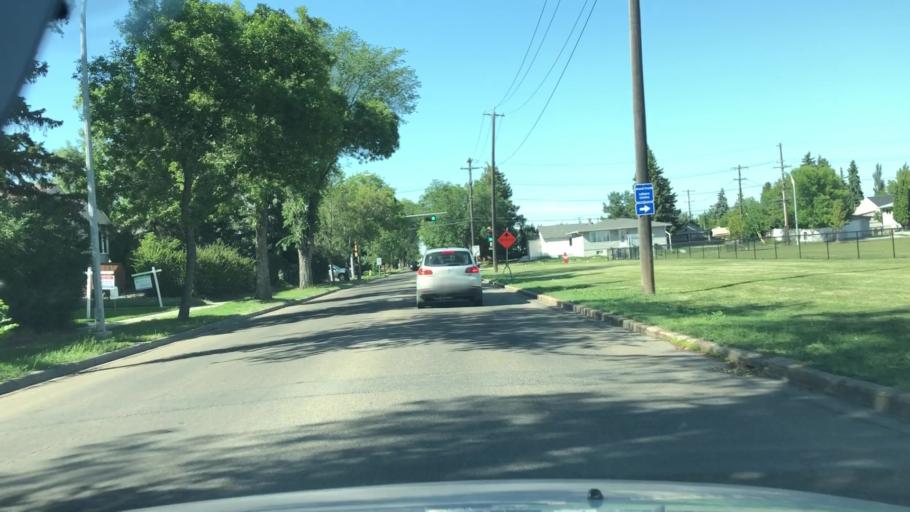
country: CA
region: Alberta
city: Edmonton
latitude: 53.5866
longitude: -113.5165
